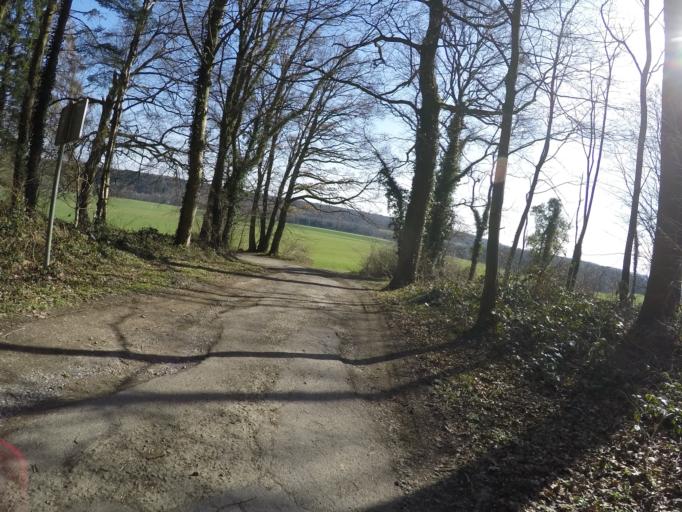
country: BE
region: Wallonia
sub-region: Province de Namur
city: Havelange
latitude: 50.4076
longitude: 5.2020
